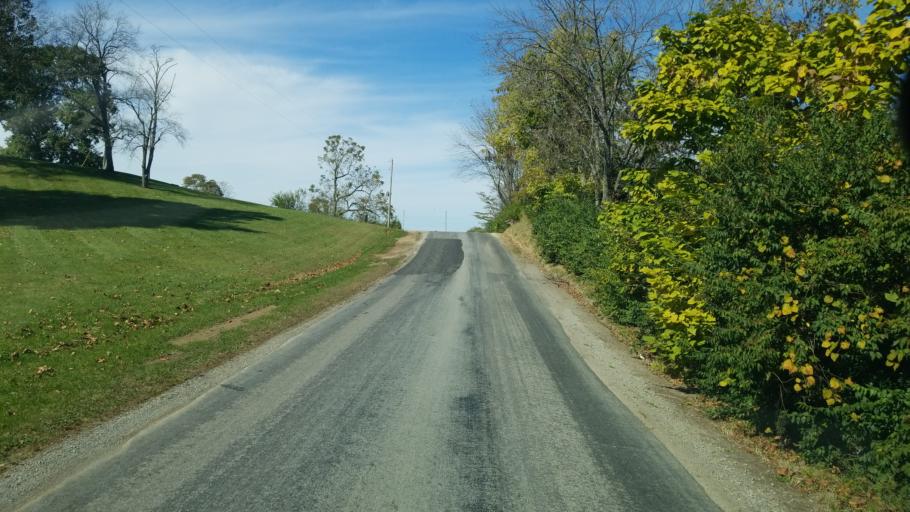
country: US
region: Ohio
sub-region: Highland County
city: Leesburg
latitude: 39.2830
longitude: -83.4771
